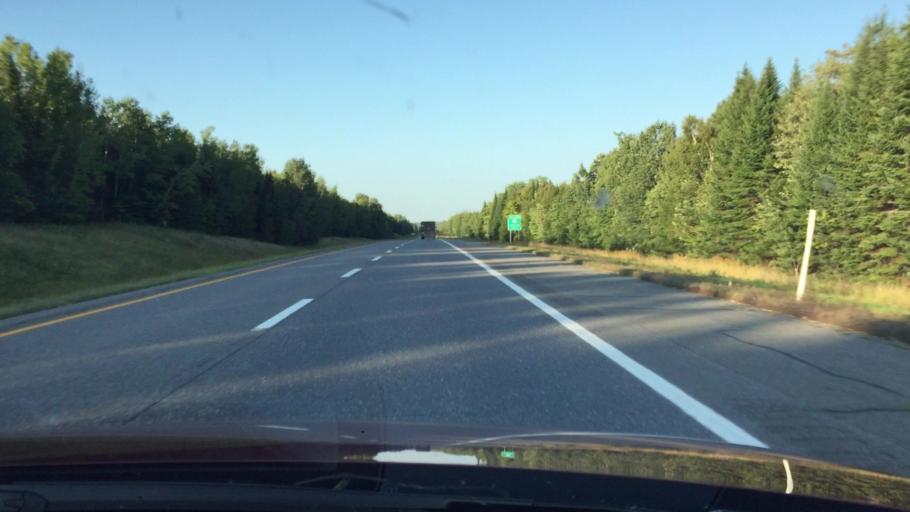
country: US
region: Maine
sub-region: Aroostook County
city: Hodgdon
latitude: 46.1266
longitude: -68.1010
